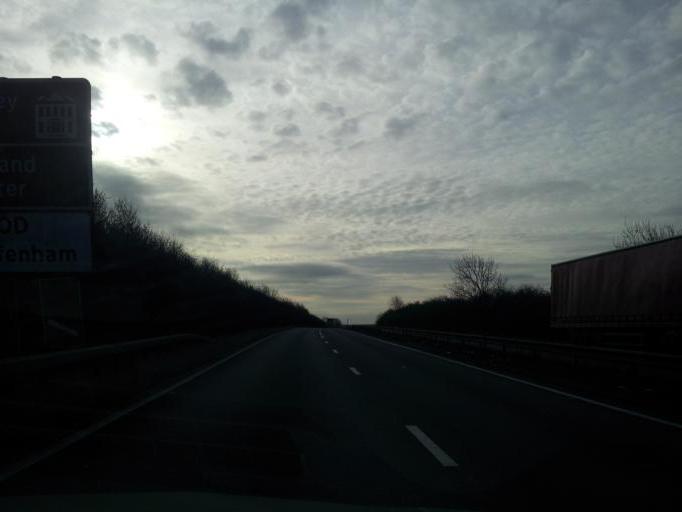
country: GB
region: England
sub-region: District of Rutland
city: Tinwell
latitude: 52.6595
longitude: -0.5173
